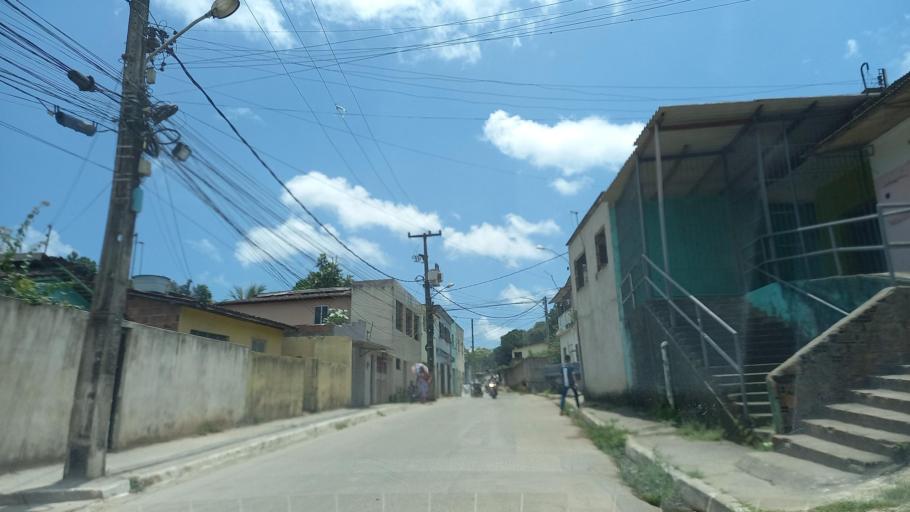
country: BR
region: Pernambuco
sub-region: Jaboatao Dos Guararapes
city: Jaboatao
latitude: -8.1728
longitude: -35.0036
